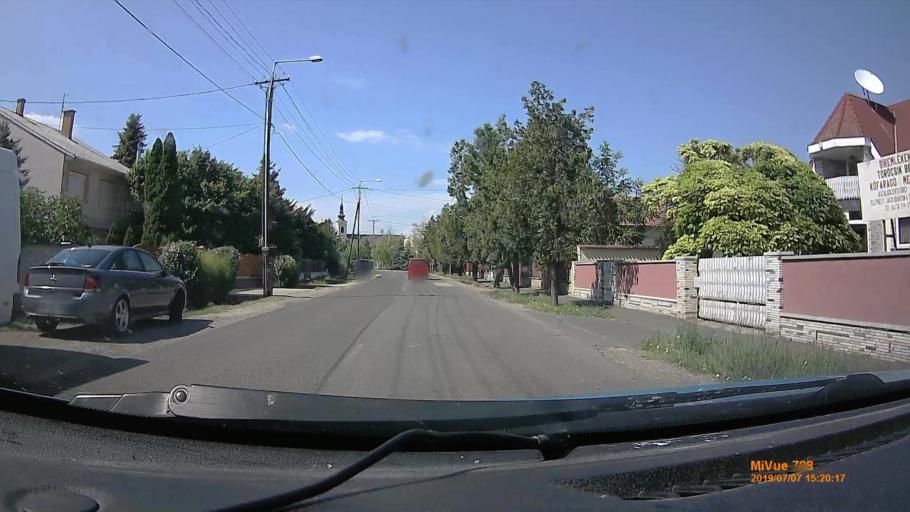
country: HU
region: Jasz-Nagykun-Szolnok
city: Jaszalsoszentgyorgy
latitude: 47.3691
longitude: 20.0921
